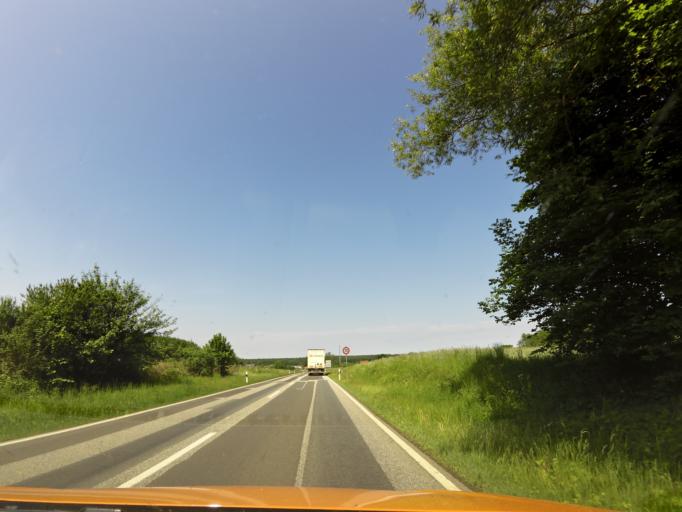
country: DE
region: Mecklenburg-Vorpommern
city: Selmsdorf
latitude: 53.8793
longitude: 10.8677
